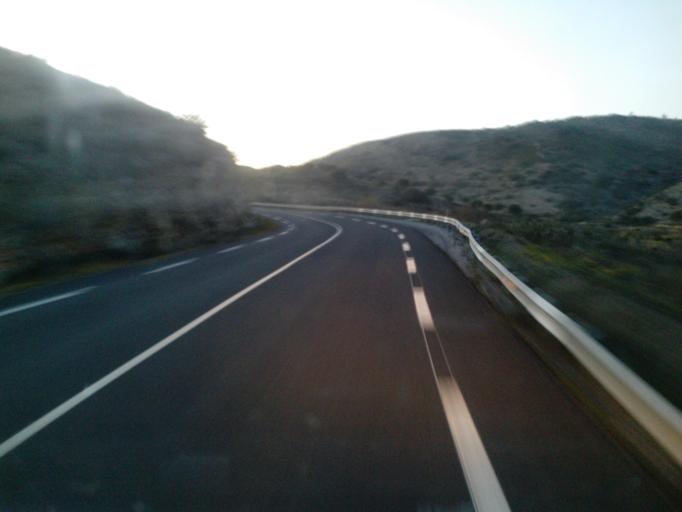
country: FR
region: Languedoc-Roussillon
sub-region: Departement des Pyrenees-Orientales
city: Estagel
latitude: 42.7765
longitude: 2.7267
